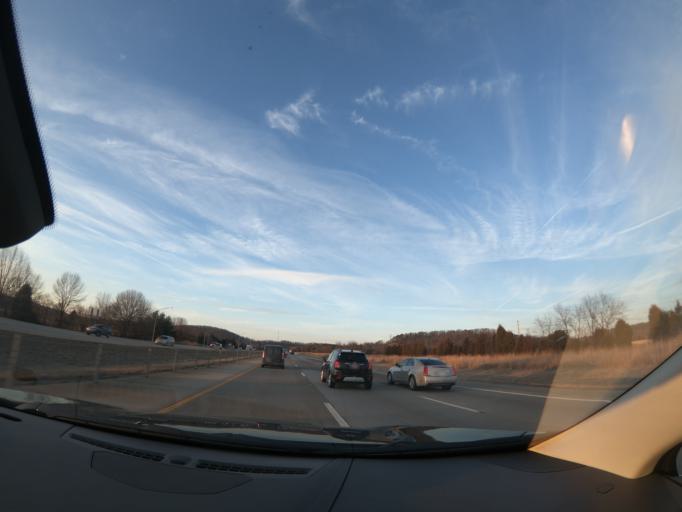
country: US
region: Kentucky
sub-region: Bullitt County
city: Shepherdsville
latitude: 37.9413
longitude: -85.6884
